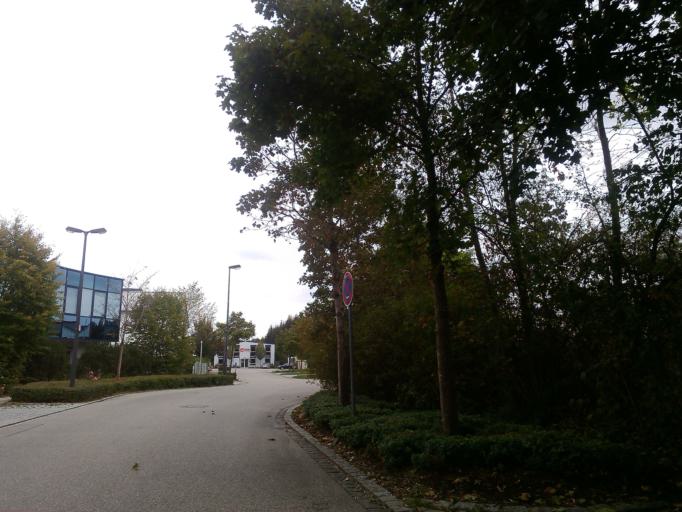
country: DE
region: Bavaria
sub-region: Upper Bavaria
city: Gauting
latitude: 48.0956
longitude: 11.3630
